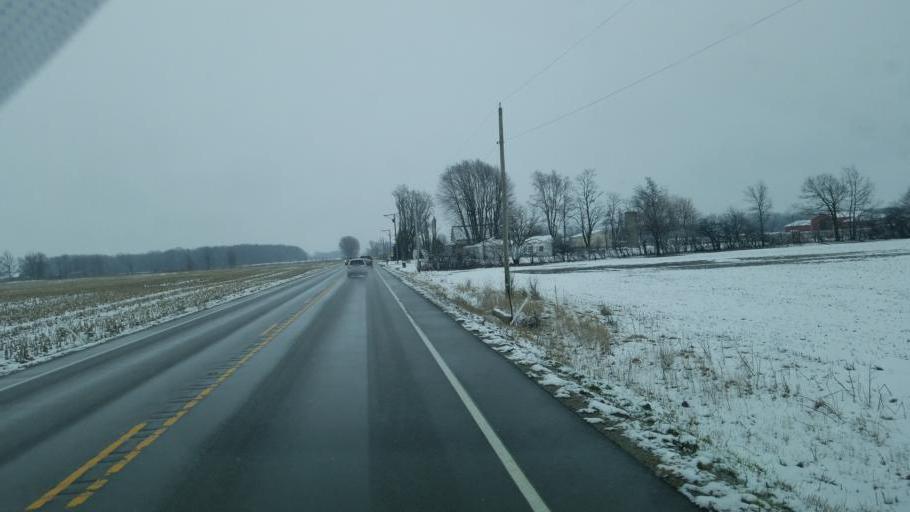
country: US
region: Indiana
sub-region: Delaware County
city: Yorktown
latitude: 40.2770
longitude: -85.4680
